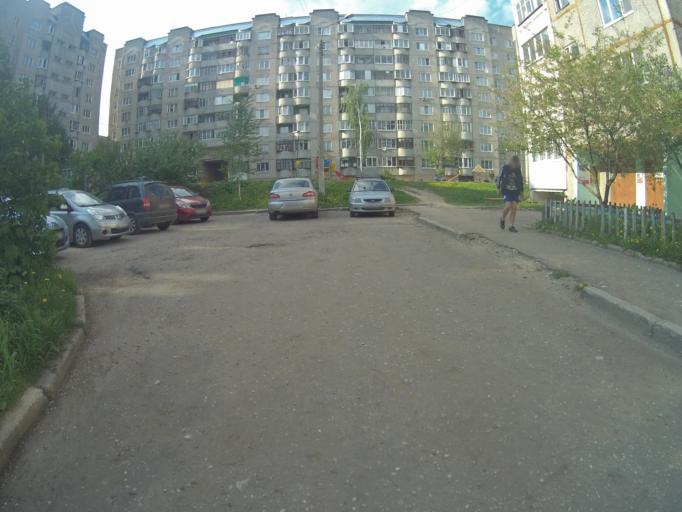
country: RU
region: Vladimir
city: Kommunar
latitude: 56.1666
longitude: 40.4471
